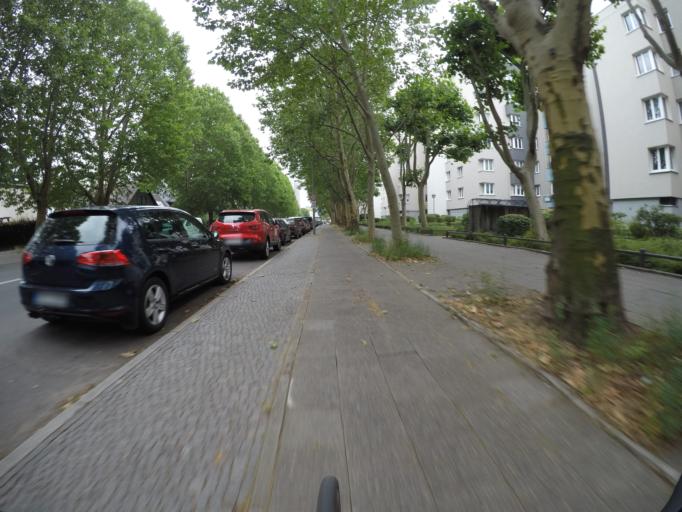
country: DE
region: Berlin
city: Markisches Viertel
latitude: 52.5960
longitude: 13.3446
